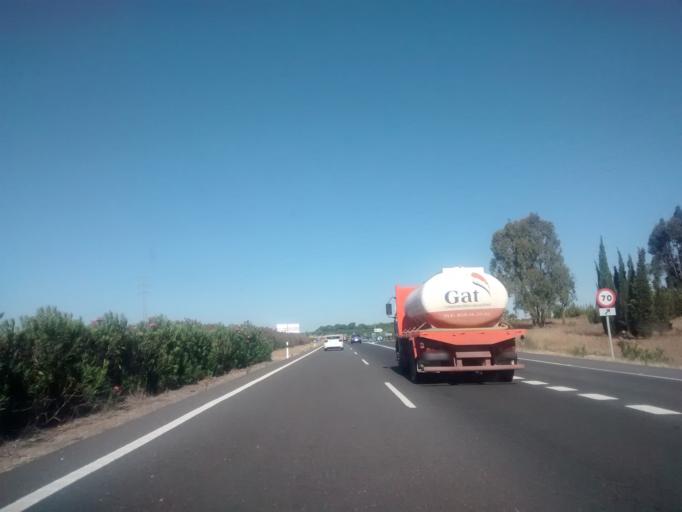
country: ES
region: Andalusia
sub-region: Provincia de Huelva
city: Aljaraque
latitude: 37.3233
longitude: -7.0728
